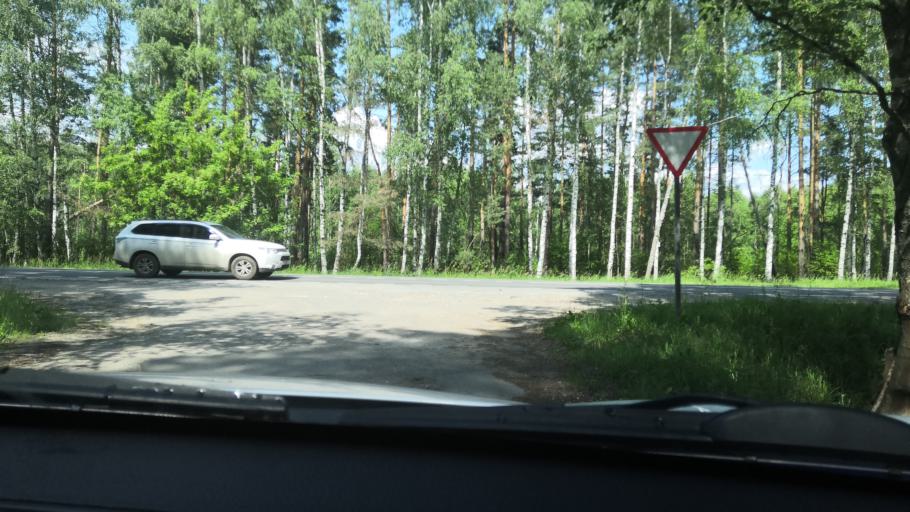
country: RU
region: Rjazan
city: Murmino
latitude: 54.5399
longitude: 40.1729
